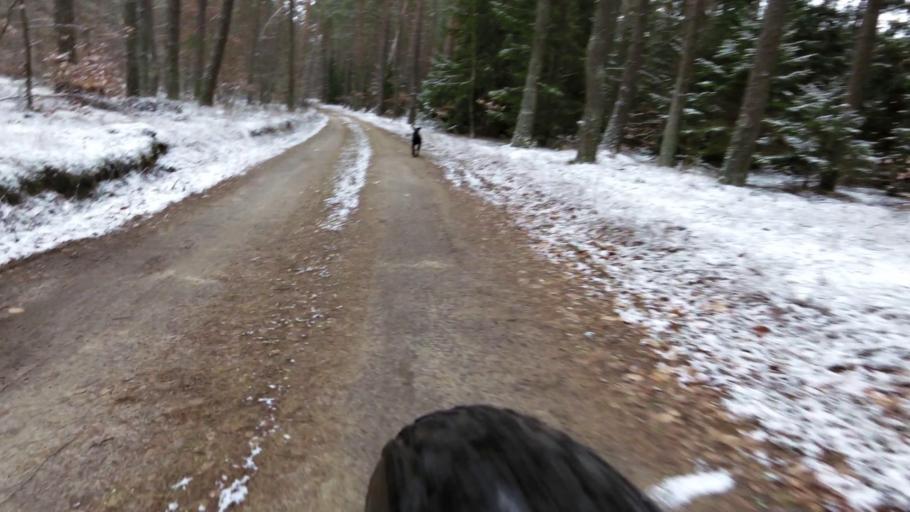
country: PL
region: West Pomeranian Voivodeship
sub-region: Powiat walecki
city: Miroslawiec
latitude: 53.3070
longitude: 16.0671
